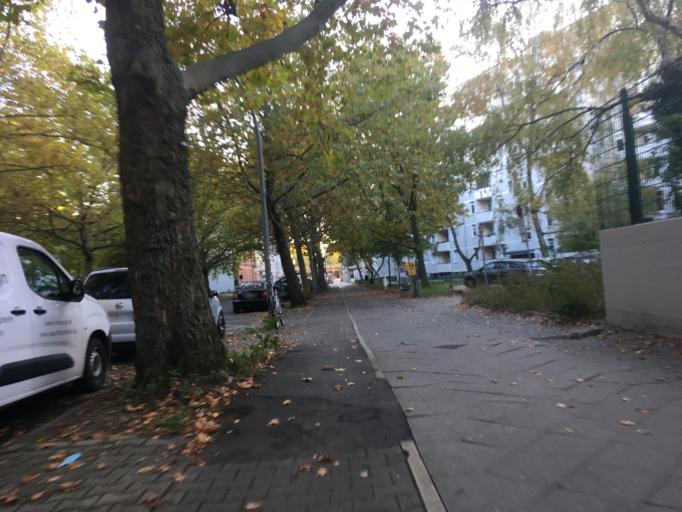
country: DE
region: Berlin
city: Bezirk Kreuzberg
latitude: 52.5007
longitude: 13.4016
